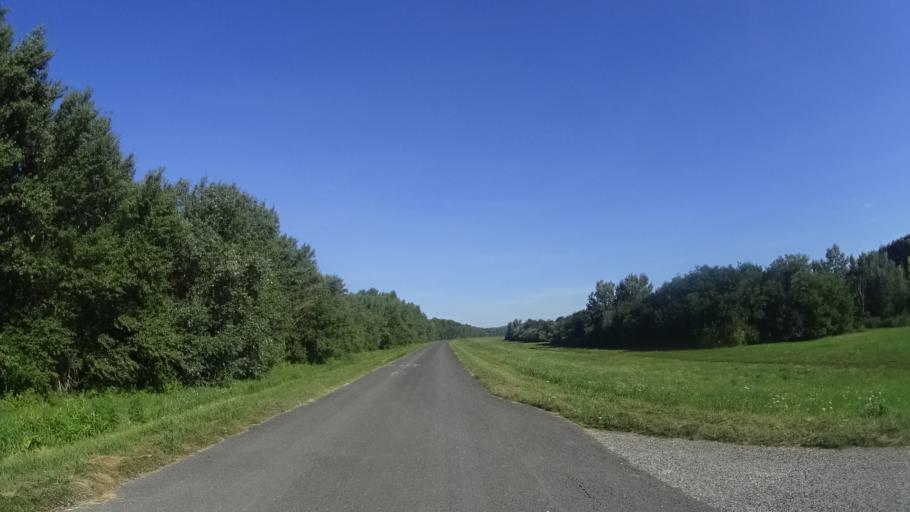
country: HU
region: Gyor-Moson-Sopron
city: Rajka
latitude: 48.0738
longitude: 17.1651
